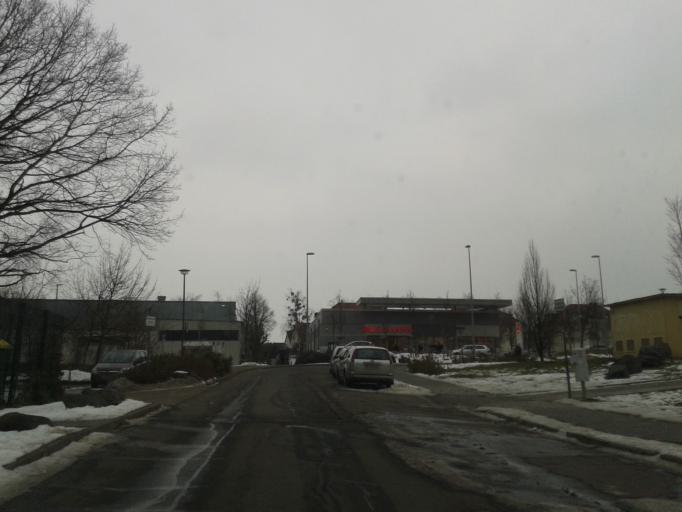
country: DE
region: Saxony
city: Dresden
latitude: 51.0204
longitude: 13.7369
